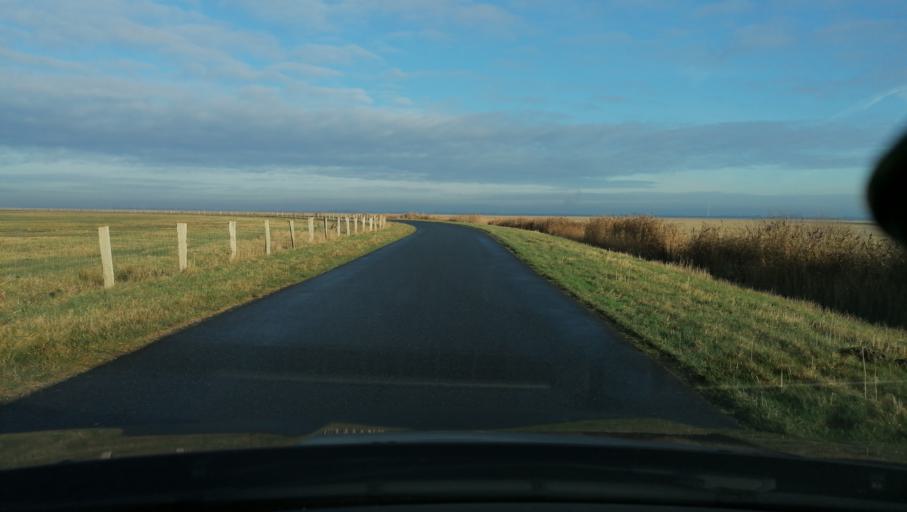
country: DE
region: Schleswig-Holstein
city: Friedrichsgabekoog
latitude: 54.1039
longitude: 8.9521
